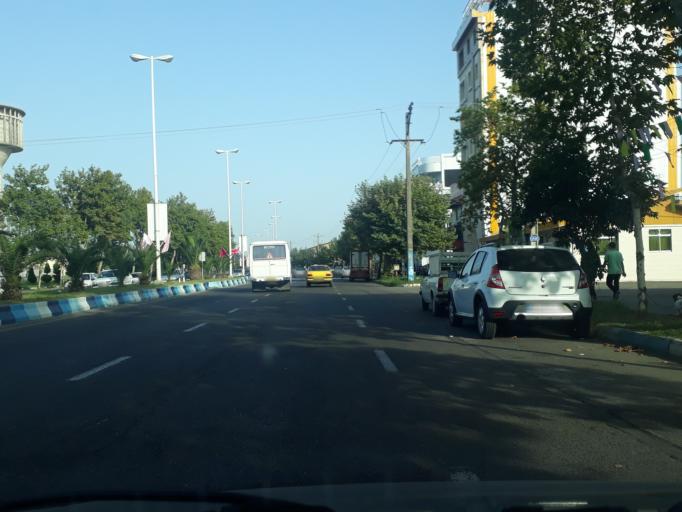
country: IR
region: Gilan
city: Bandar-e Anzali
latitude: 37.4602
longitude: 49.4951
